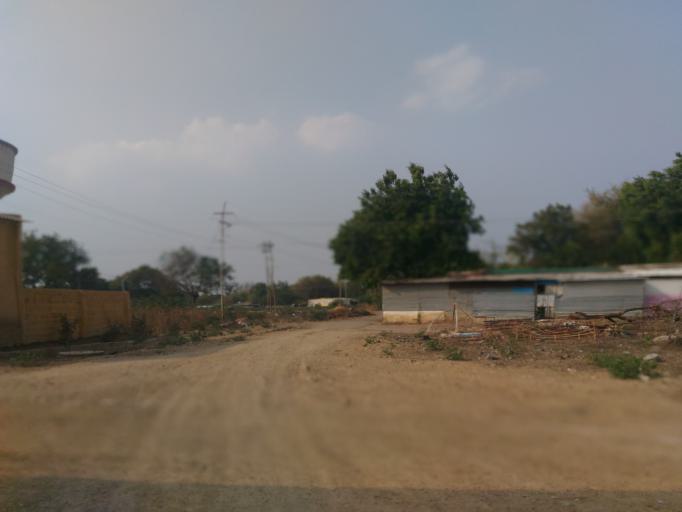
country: IN
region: Karnataka
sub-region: Raichur
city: Lingsugur
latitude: 16.1910
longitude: 76.6615
